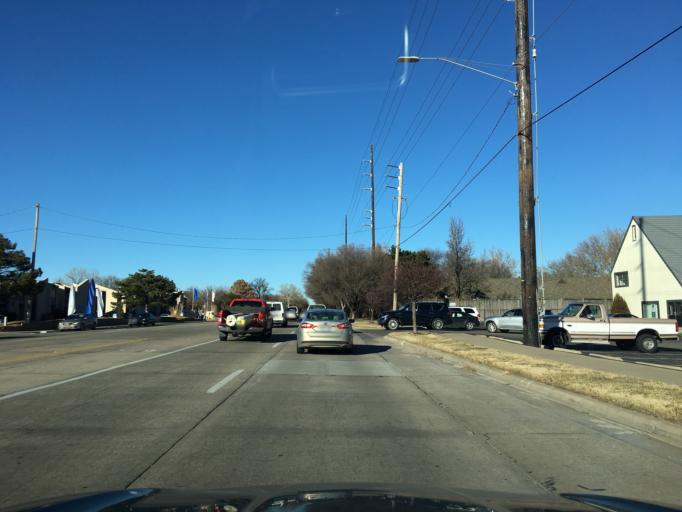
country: US
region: Kansas
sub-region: Sedgwick County
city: Bellaire
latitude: 37.6948
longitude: -97.2445
